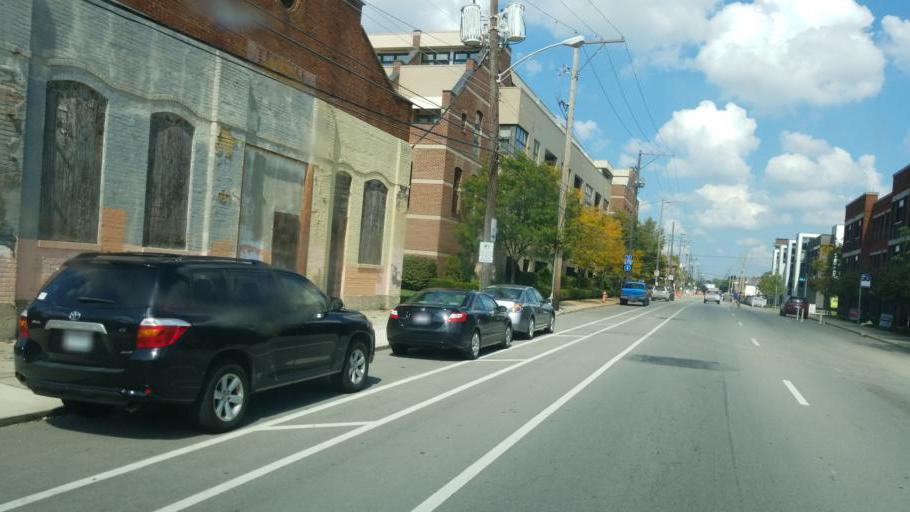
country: US
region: Ohio
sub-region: Franklin County
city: Columbus
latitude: 39.9790
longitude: -82.9981
